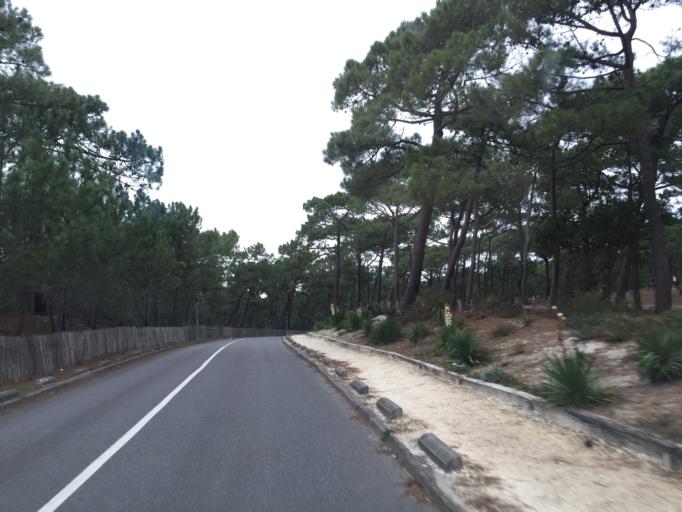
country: FR
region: Aquitaine
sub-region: Departement de la Gironde
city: Lacanau
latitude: 45.0092
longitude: -1.1954
